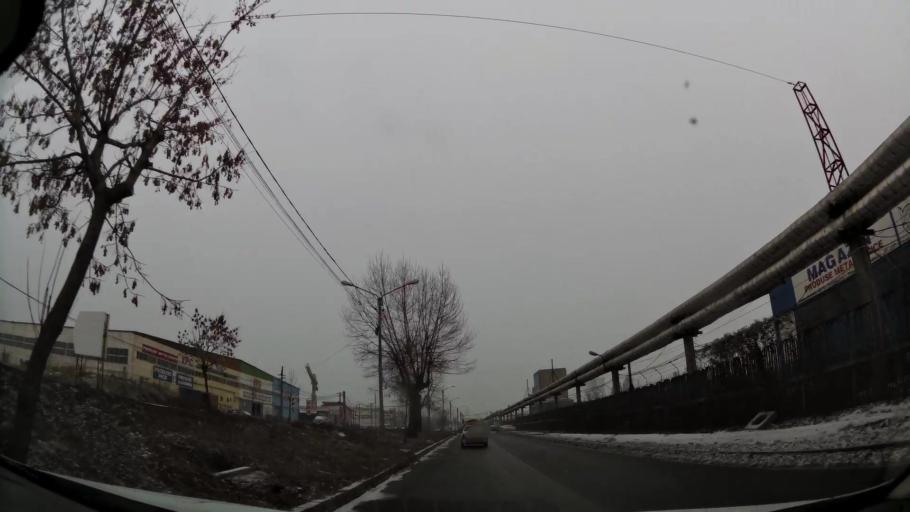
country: RO
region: Dambovita
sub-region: Municipiul Targoviste
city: Targoviste
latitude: 44.9100
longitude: 25.4579
